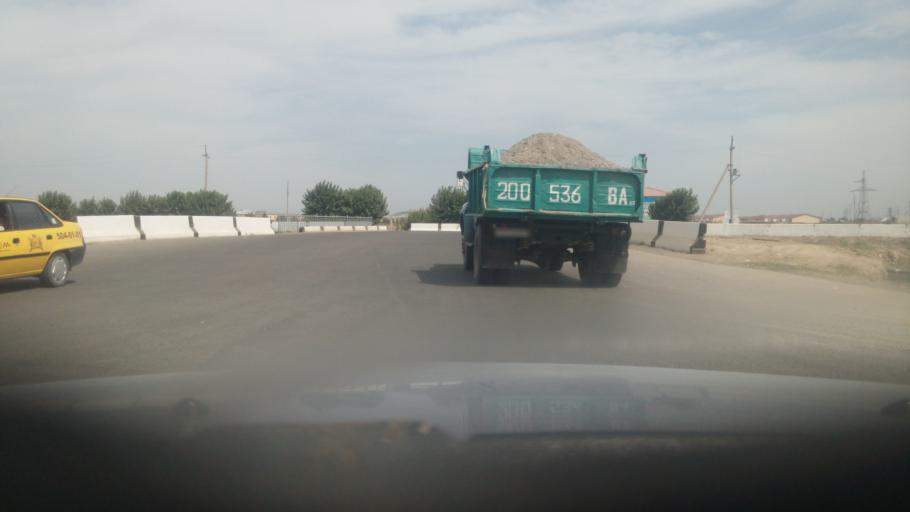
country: UZ
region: Sirdaryo
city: Guliston
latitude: 40.5172
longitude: 68.7926
